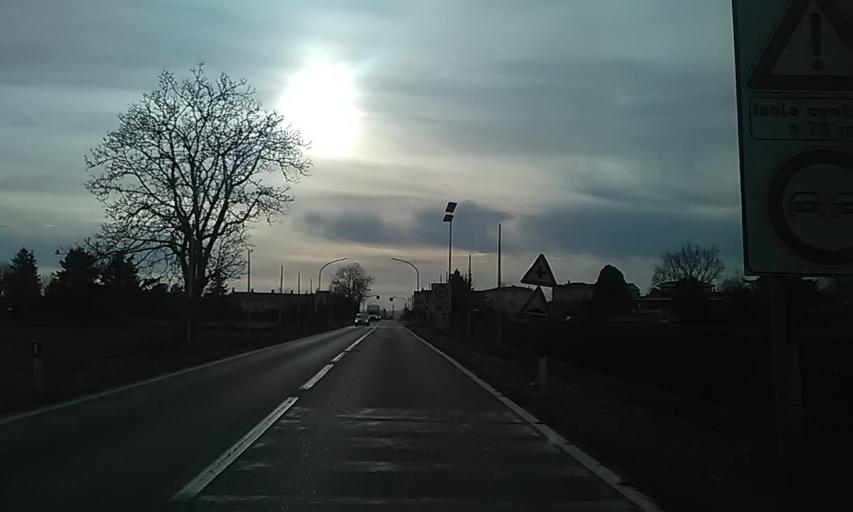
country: IT
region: Piedmont
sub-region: Provincia di Torino
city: Villareggia
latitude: 45.2765
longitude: 7.9834
